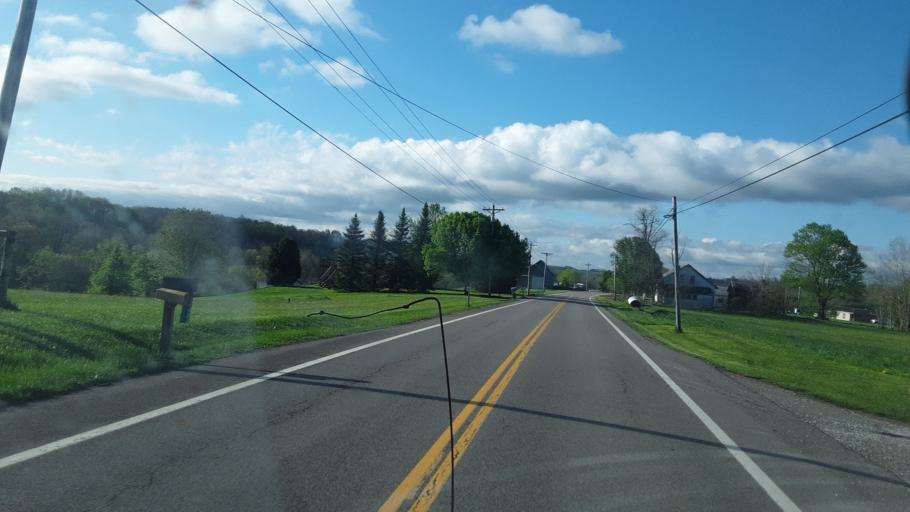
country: US
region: Ohio
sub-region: Muskingum County
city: New Concord
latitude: 39.9235
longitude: -81.6787
